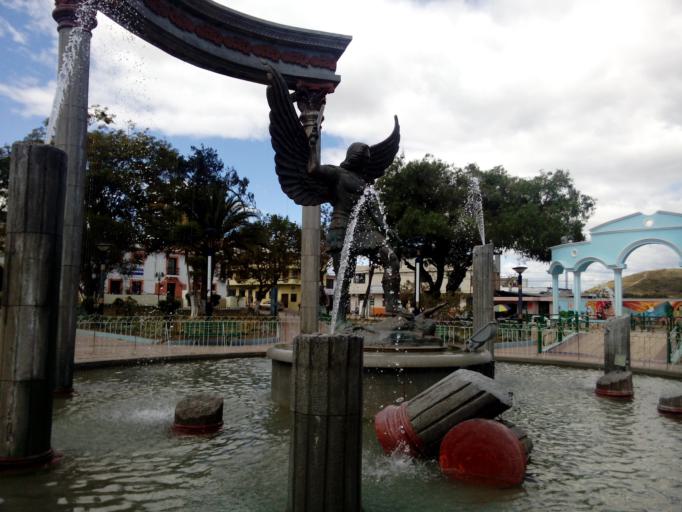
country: EC
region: Imbabura
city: Atuntaqui
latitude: 0.4172
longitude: -78.1942
